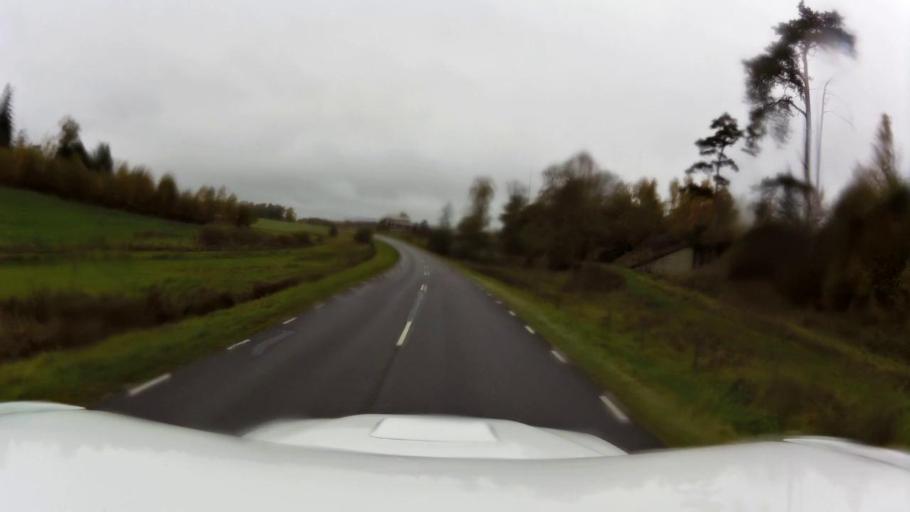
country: SE
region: OEstergoetland
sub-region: Norrkopings Kommun
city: Kimstad
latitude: 58.4073
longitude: 15.9378
